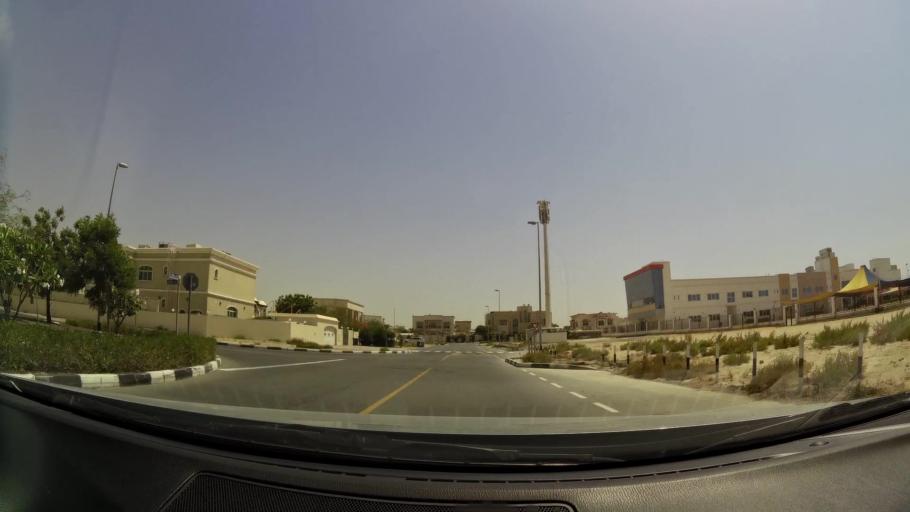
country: AE
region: Dubai
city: Dubai
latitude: 25.1075
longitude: 55.2126
